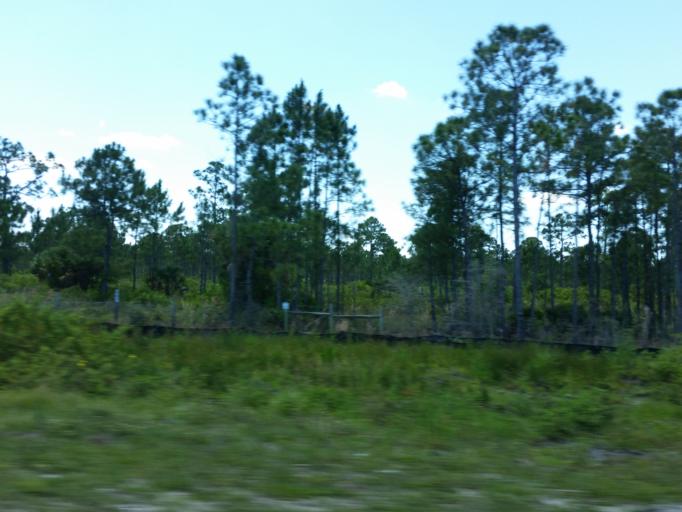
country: US
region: Florida
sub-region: Sarasota County
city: Warm Mineral Springs
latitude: 27.0999
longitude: -82.2746
